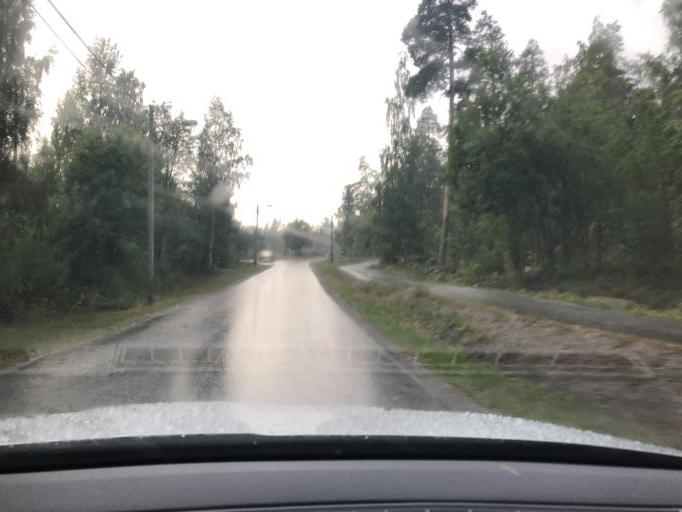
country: SE
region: Vaesternorrland
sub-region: Sundsvalls Kommun
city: Sundsvall
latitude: 62.3997
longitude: 17.3064
